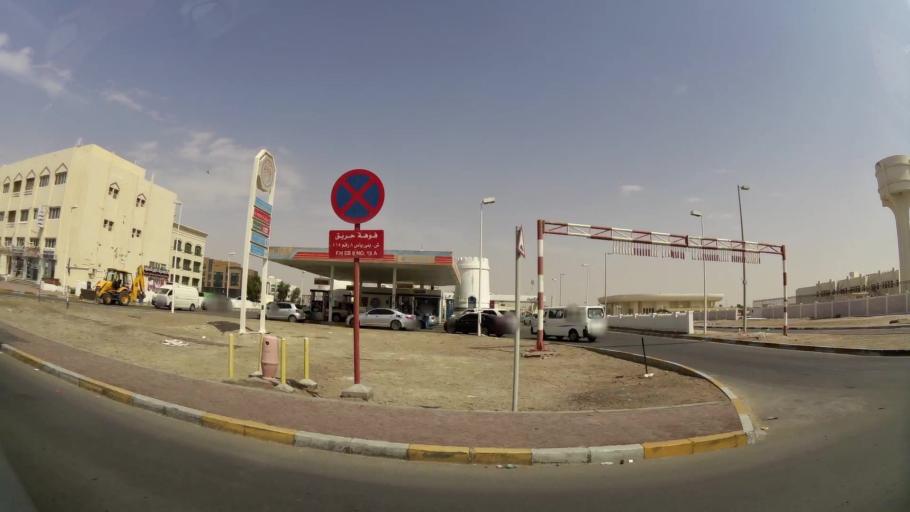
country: AE
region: Abu Dhabi
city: Abu Dhabi
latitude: 24.2942
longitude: 54.6390
